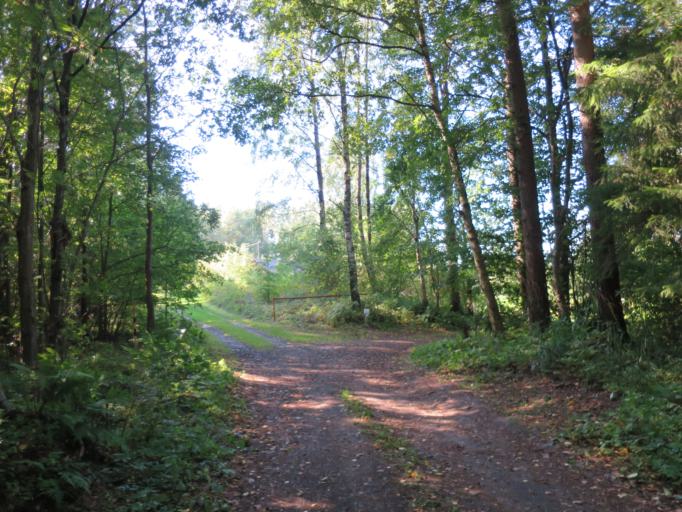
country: LV
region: Riga
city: Jaunciems
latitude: 57.0735
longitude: 24.2217
